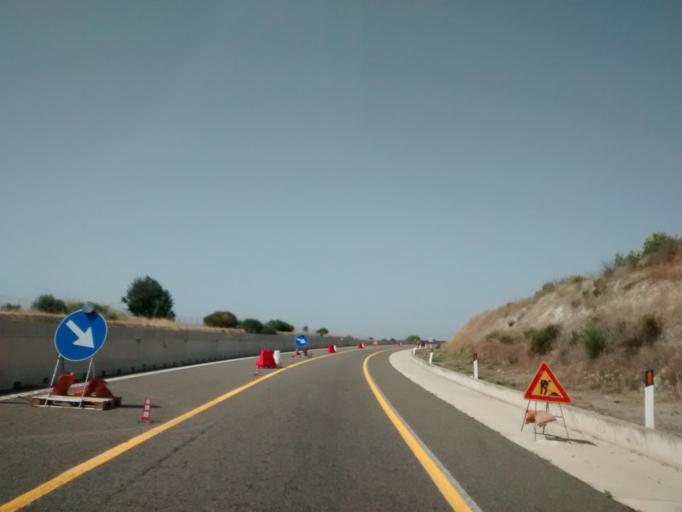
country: IT
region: Sardinia
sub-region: Provincia di Cagliari
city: Quartu Sant'Elena
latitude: 39.2407
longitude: 9.2898
